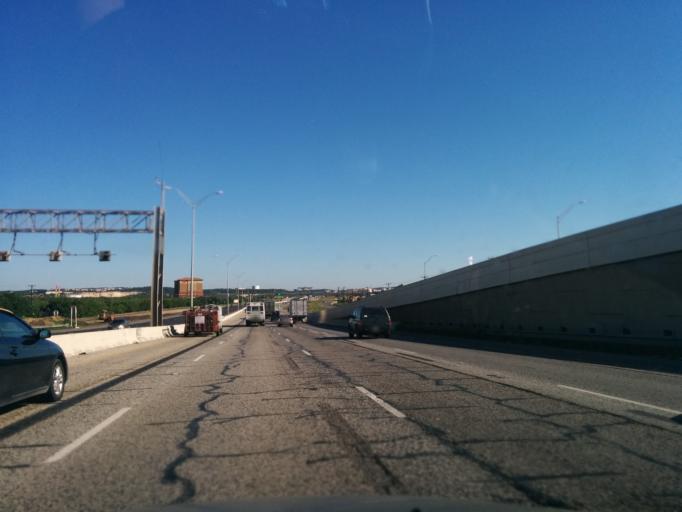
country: US
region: Texas
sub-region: Bexar County
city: Shavano Park
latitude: 29.5798
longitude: -98.5961
